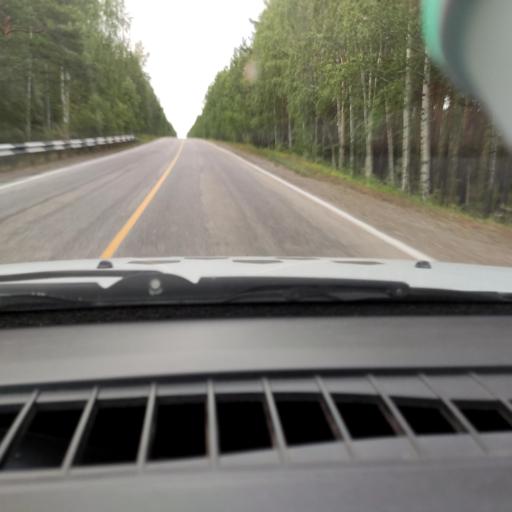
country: RU
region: Chelyabinsk
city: Ozersk
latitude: 55.8126
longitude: 60.6369
